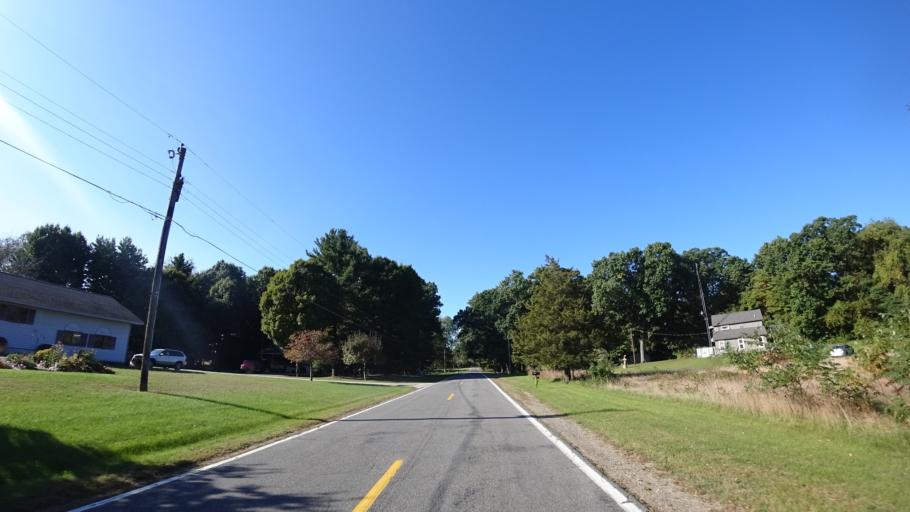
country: US
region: Michigan
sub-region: Berrien County
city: Benton Heights
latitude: 42.1594
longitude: -86.4115
